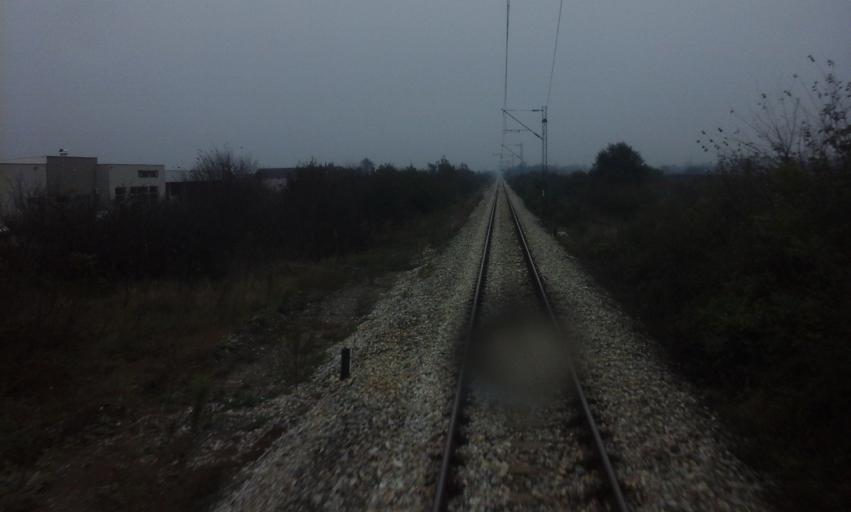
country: RS
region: Central Serbia
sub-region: Pomoravski Okrug
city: Cuprija
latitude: 43.9015
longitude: 21.3793
